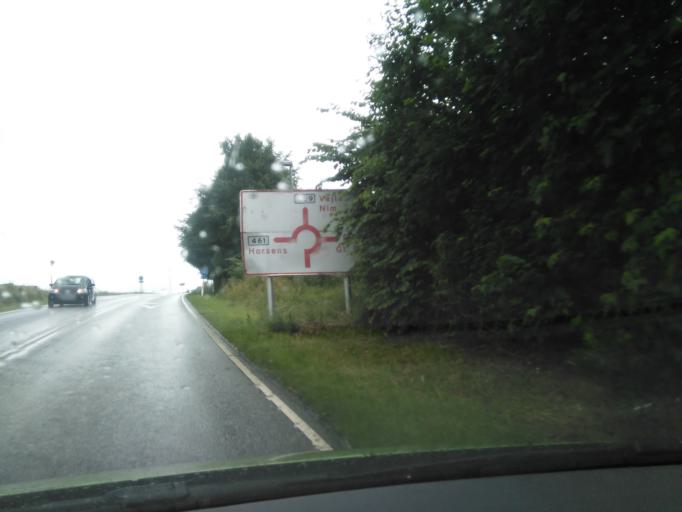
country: DK
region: Central Jutland
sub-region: Skanderborg Kommune
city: Ry
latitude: 55.9658
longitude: 9.7454
